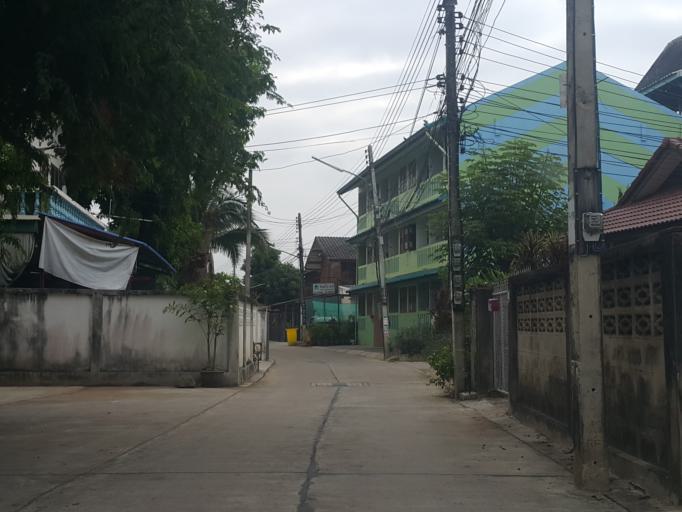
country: TH
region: Lampang
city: Lampang
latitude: 18.2930
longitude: 99.5082
